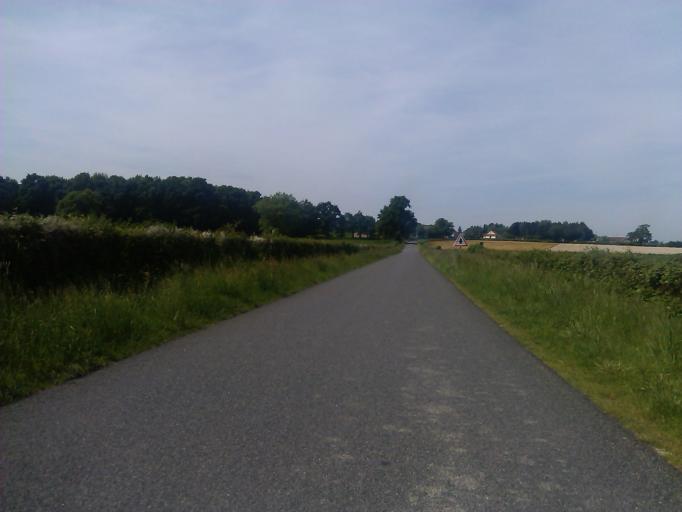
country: FR
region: Auvergne
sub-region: Departement de l'Allier
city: Vallon-en-Sully
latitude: 46.6048
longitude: 2.5198
